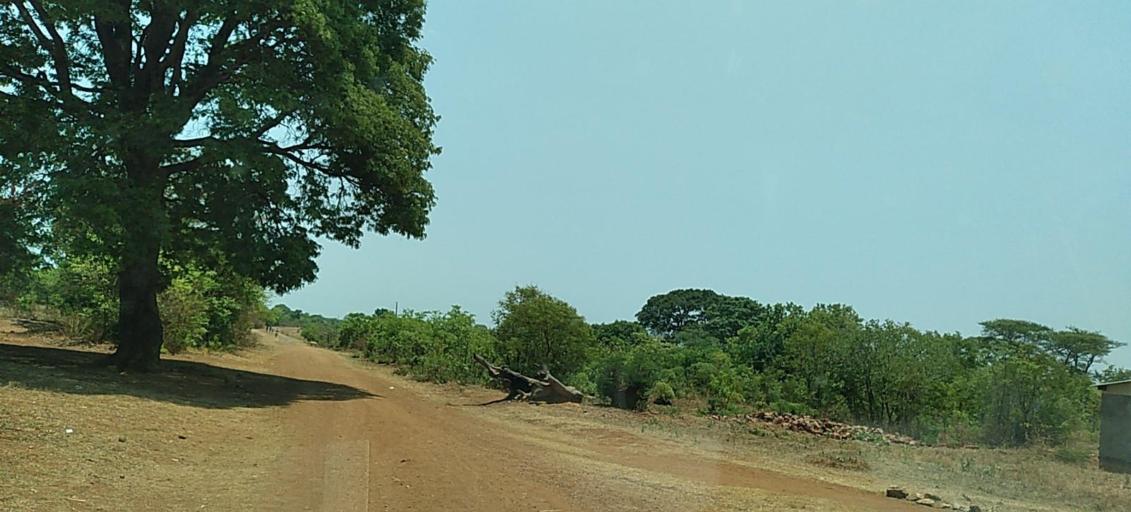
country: ZM
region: Copperbelt
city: Mpongwe
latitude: -13.8333
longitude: 27.8381
